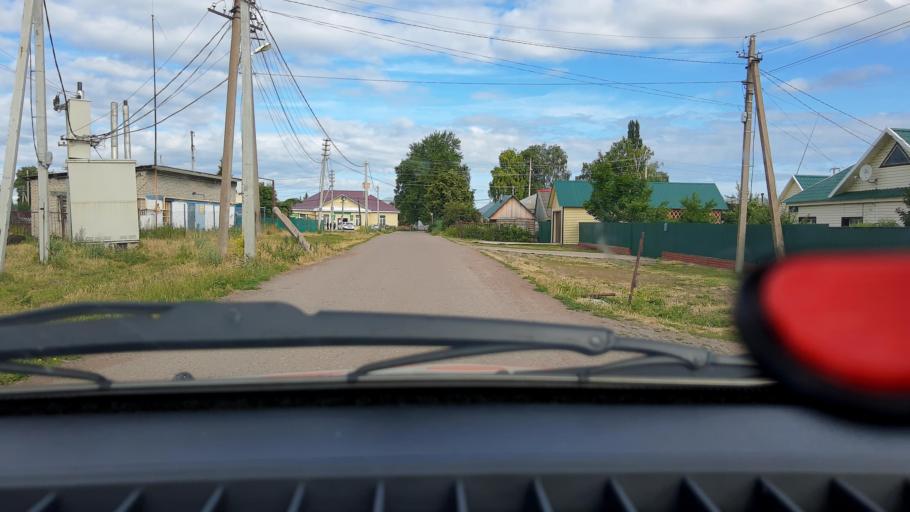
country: RU
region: Bashkortostan
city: Kabakovo
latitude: 54.5167
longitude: 55.9476
